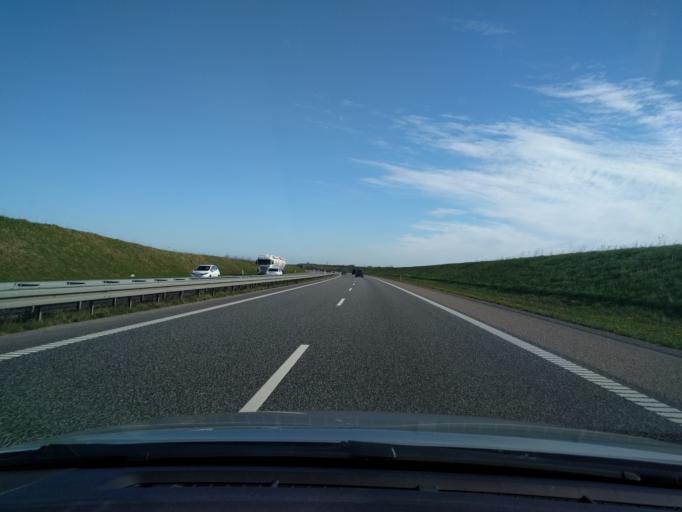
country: DK
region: South Denmark
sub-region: Vejle Kommune
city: Vejle
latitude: 55.7756
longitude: 9.5686
